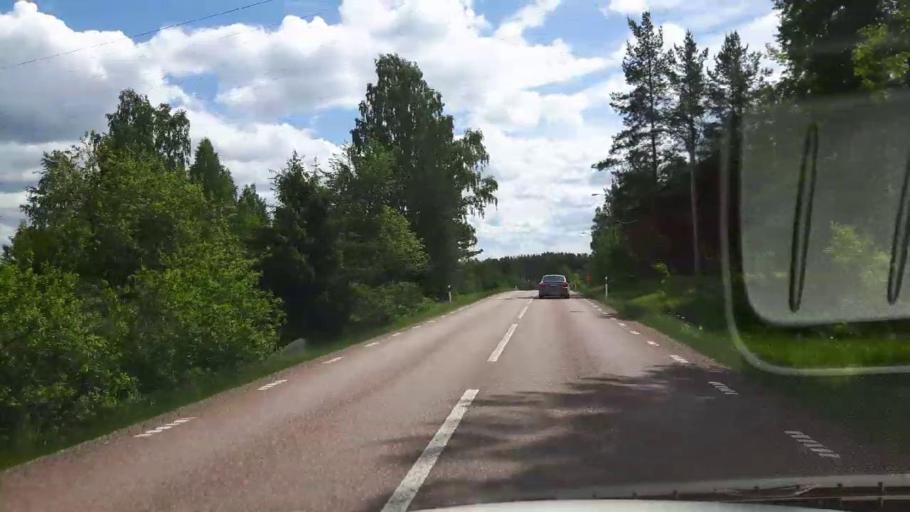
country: SE
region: Dalarna
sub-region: Saters Kommun
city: Saeter
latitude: 60.4225
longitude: 15.8432
